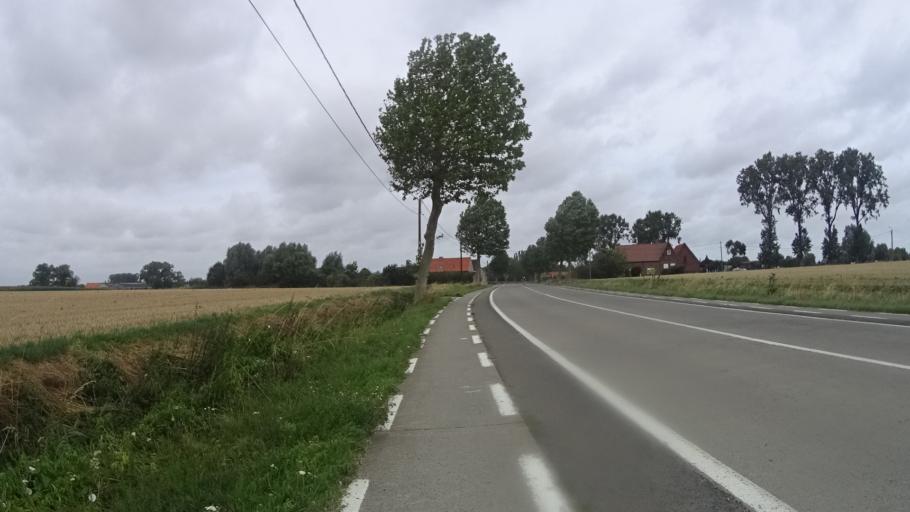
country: BE
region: Flanders
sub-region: Provincie West-Vlaanderen
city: Diksmuide
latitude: 51.0555
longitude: 2.8963
